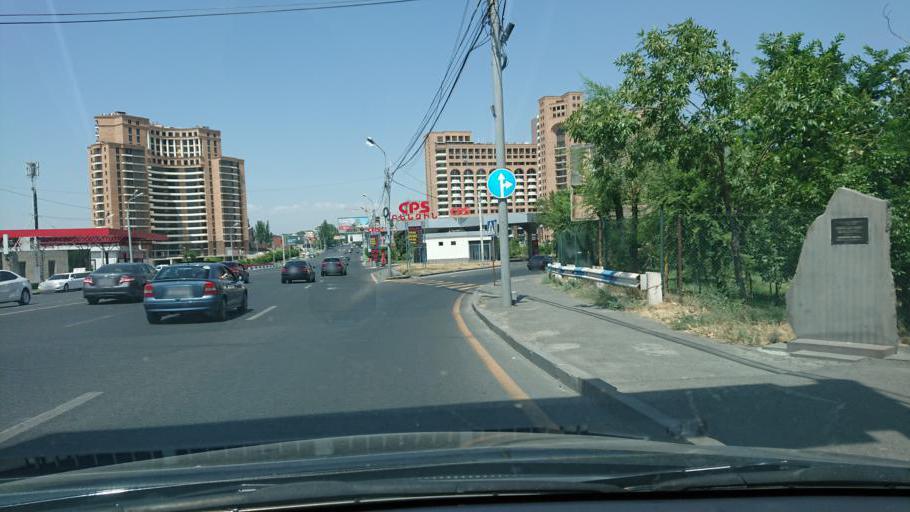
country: AM
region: Yerevan
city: Yerevan
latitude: 40.2116
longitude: 44.4918
